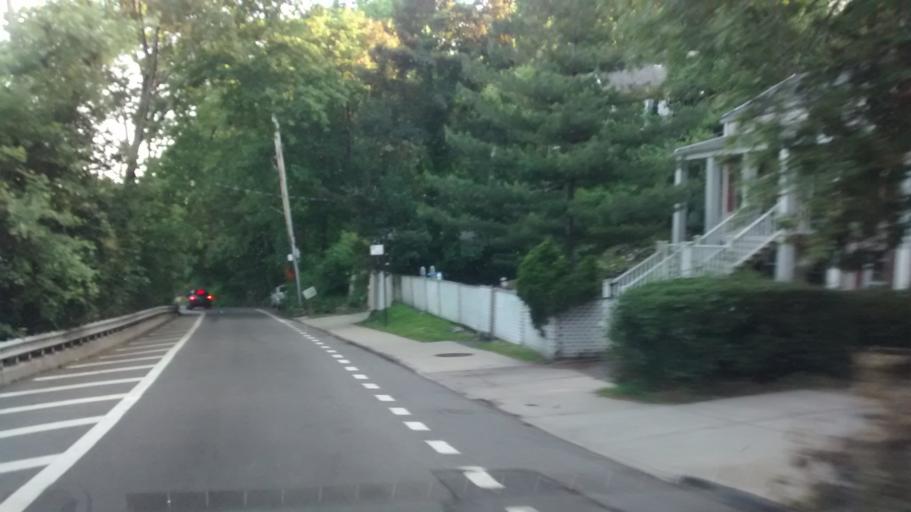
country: US
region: New Jersey
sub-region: Hudson County
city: Bayonne
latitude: 40.6276
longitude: -74.0838
